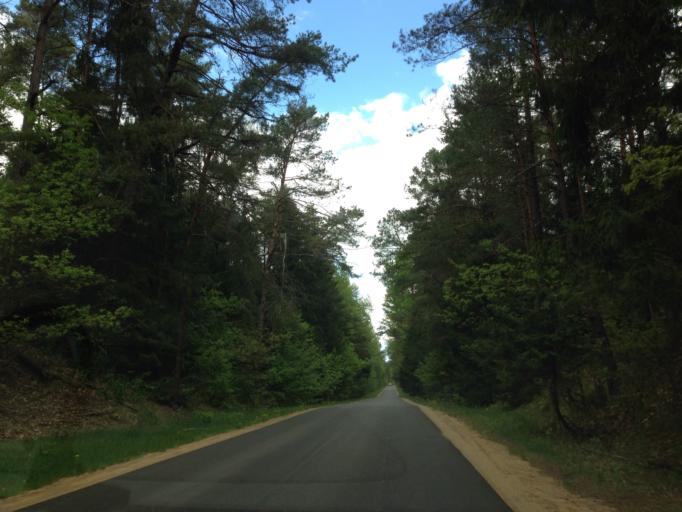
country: PL
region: Podlasie
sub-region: Powiat grajewski
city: Radzilow
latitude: 53.3422
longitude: 22.5980
